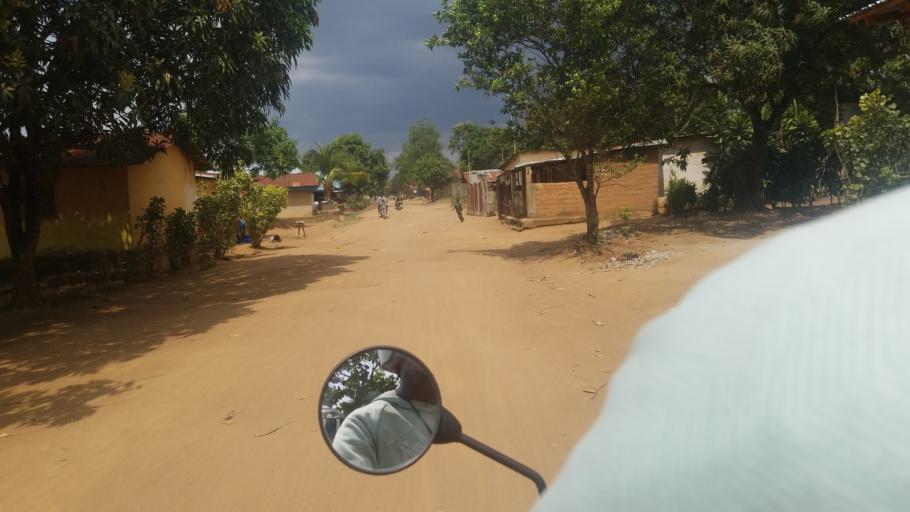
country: SL
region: Western Area
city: Waterloo
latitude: 8.3200
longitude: -13.0464
